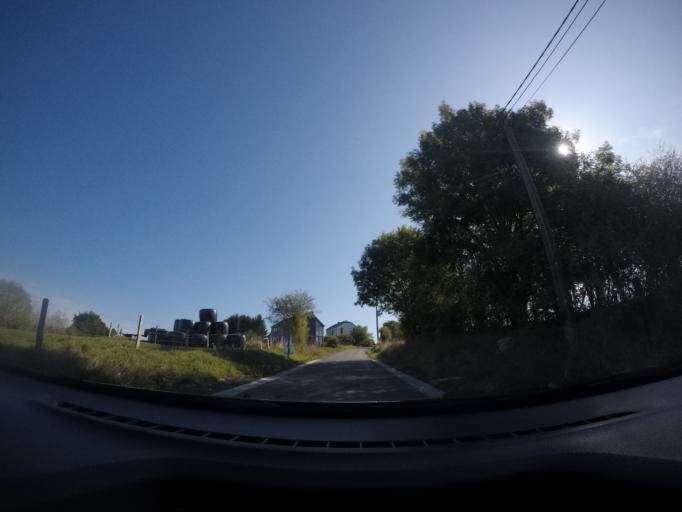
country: BE
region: Wallonia
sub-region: Province du Luxembourg
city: Fauvillers
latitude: 49.9084
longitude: 5.6909
